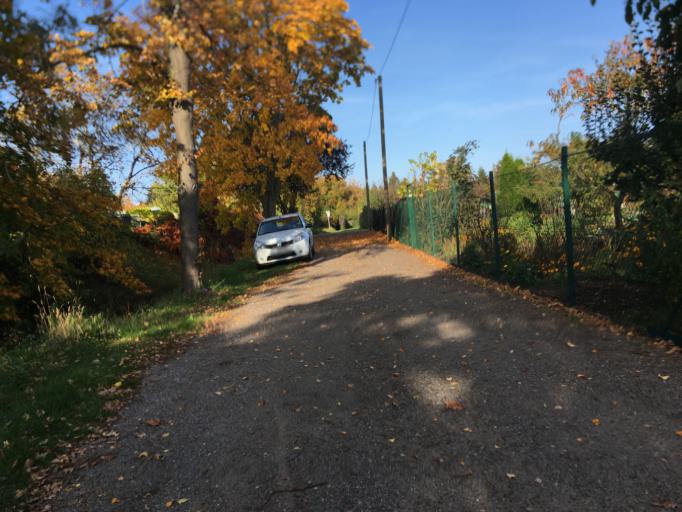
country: DE
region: Berlin
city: Rosenthal
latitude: 52.5939
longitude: 13.3896
